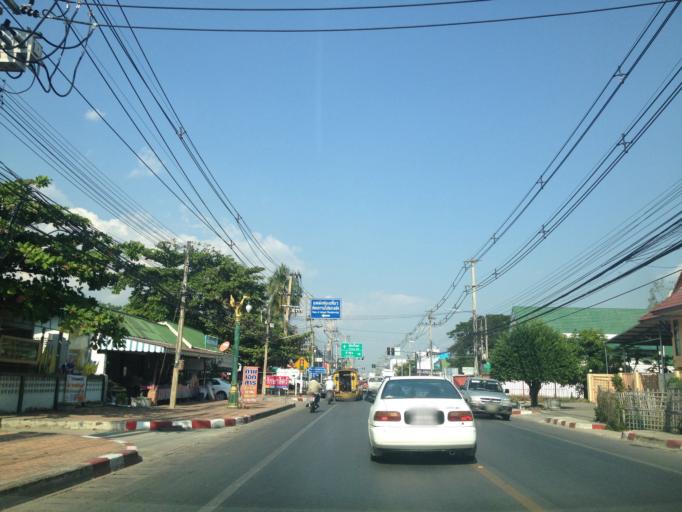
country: TH
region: Chiang Mai
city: San Pa Tong
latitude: 18.6298
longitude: 98.8968
